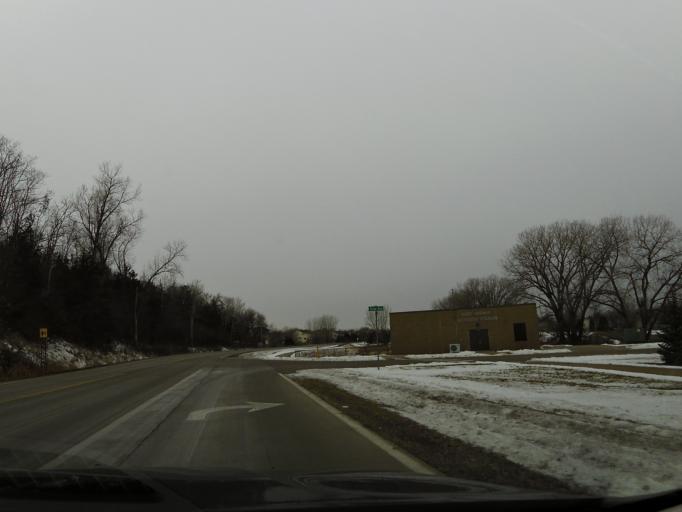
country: US
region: Minnesota
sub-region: Scott County
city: Jordan
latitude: 44.6535
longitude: -93.6358
